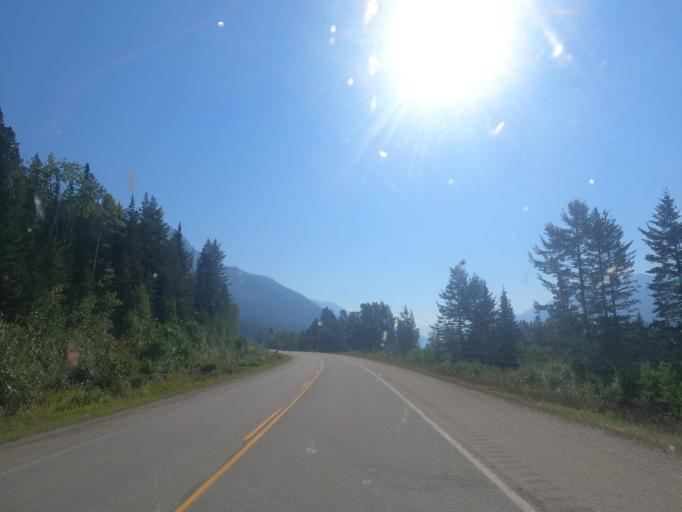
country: CA
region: Alberta
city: Jasper Park Lodge
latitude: 52.9733
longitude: -118.9540
